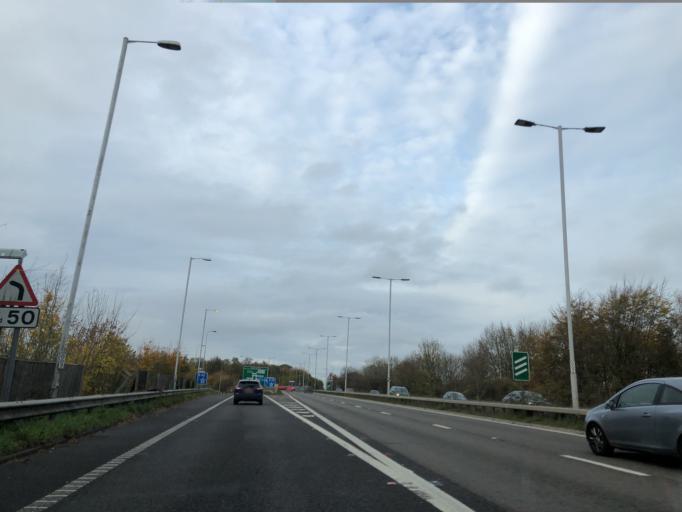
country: GB
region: England
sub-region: Buckinghamshire
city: High Wycombe
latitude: 51.6085
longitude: -0.7666
